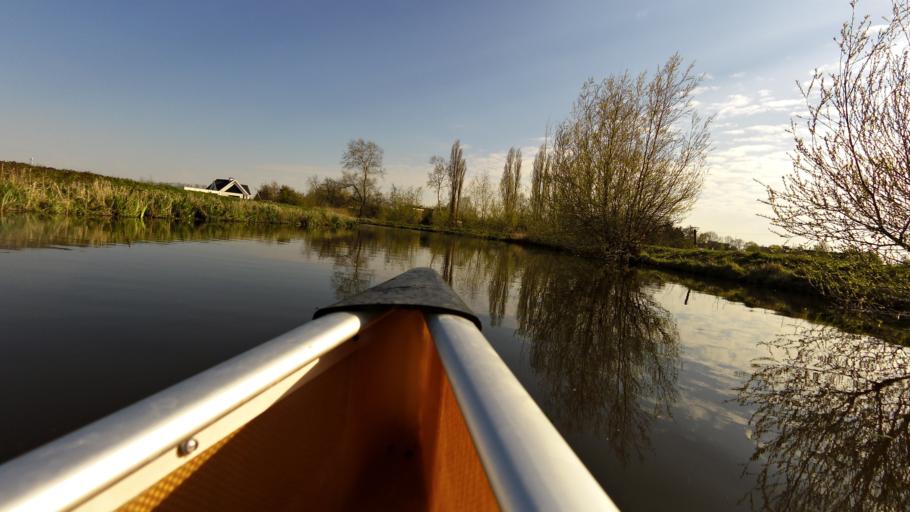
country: NL
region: South Holland
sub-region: Gemeente Teylingen
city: Sassenheim
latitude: 52.2267
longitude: 4.5366
